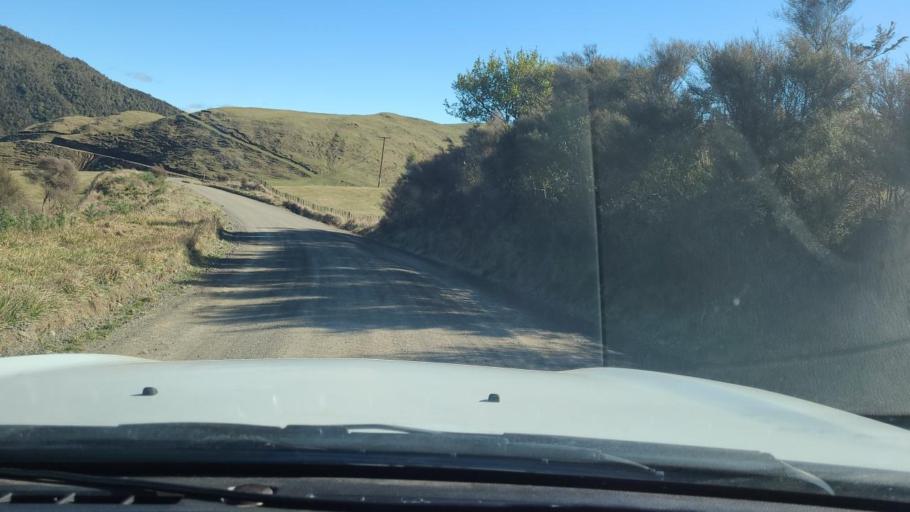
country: NZ
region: Hawke's Bay
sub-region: Napier City
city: Taradale
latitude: -39.2395
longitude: 176.4972
